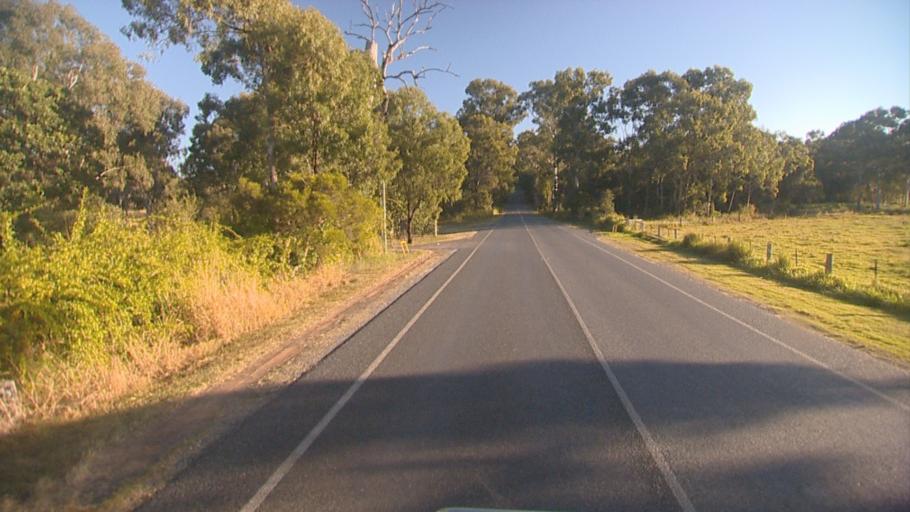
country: AU
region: Queensland
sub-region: Logan
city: Logan Reserve
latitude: -27.7213
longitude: 153.1092
